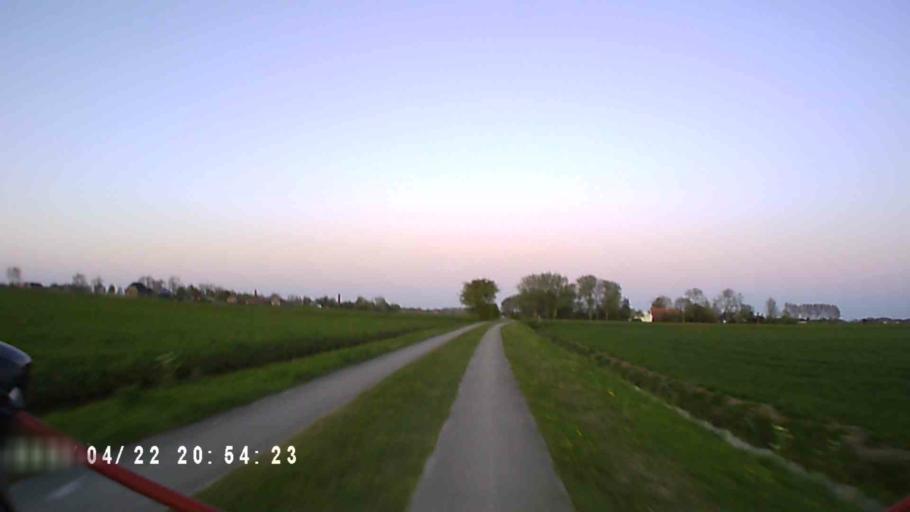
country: NL
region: Groningen
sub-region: Gemeente Winsum
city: Winsum
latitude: 53.3323
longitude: 6.5556
